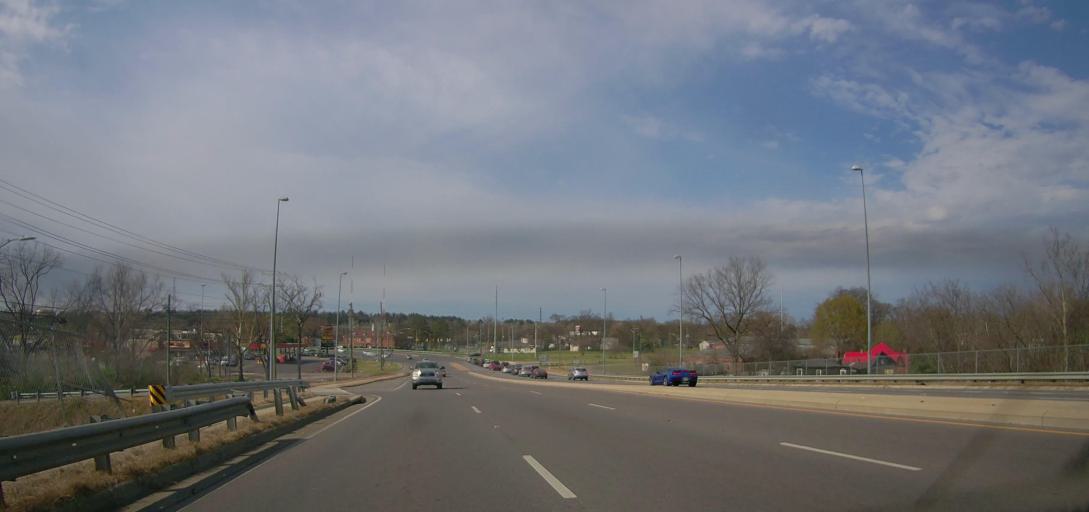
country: US
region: Alabama
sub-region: Jefferson County
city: Birmingham
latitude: 33.5278
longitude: -86.8505
